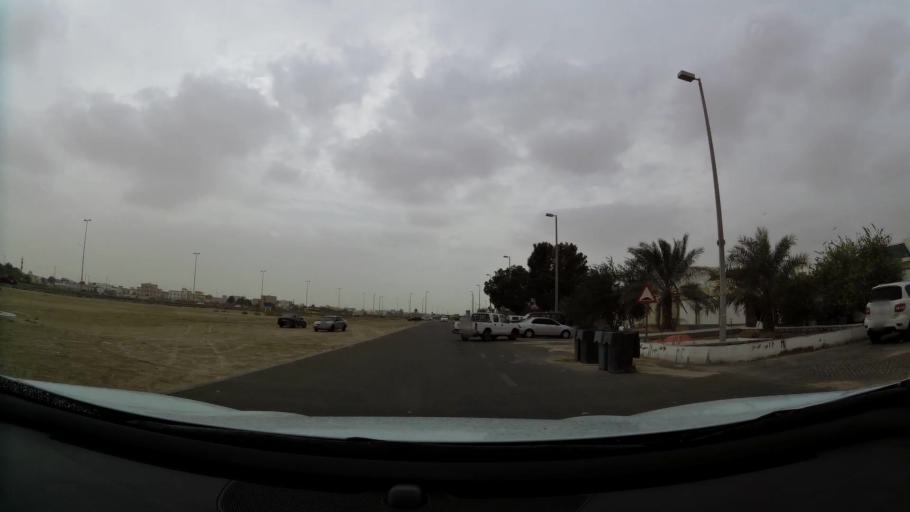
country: AE
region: Abu Dhabi
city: Abu Dhabi
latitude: 24.3614
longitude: 54.6579
